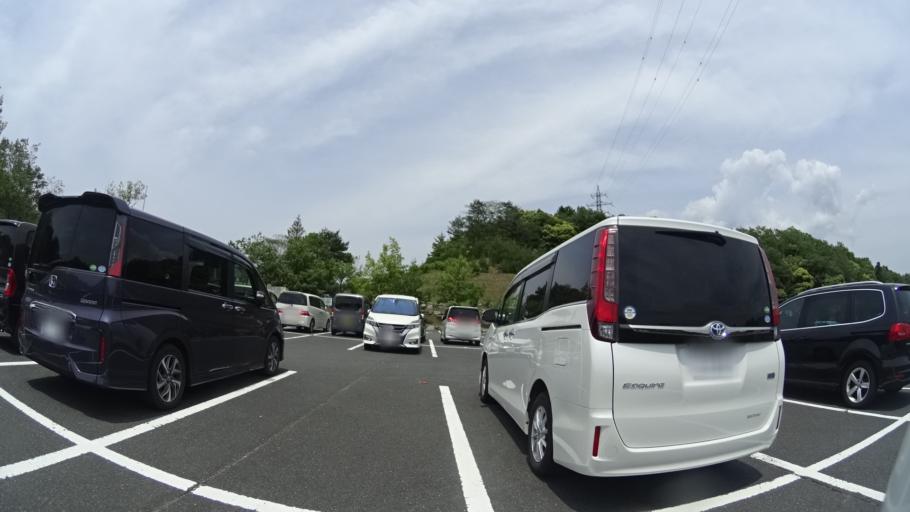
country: JP
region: Kyoto
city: Miyazu
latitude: 35.6735
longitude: 135.0683
